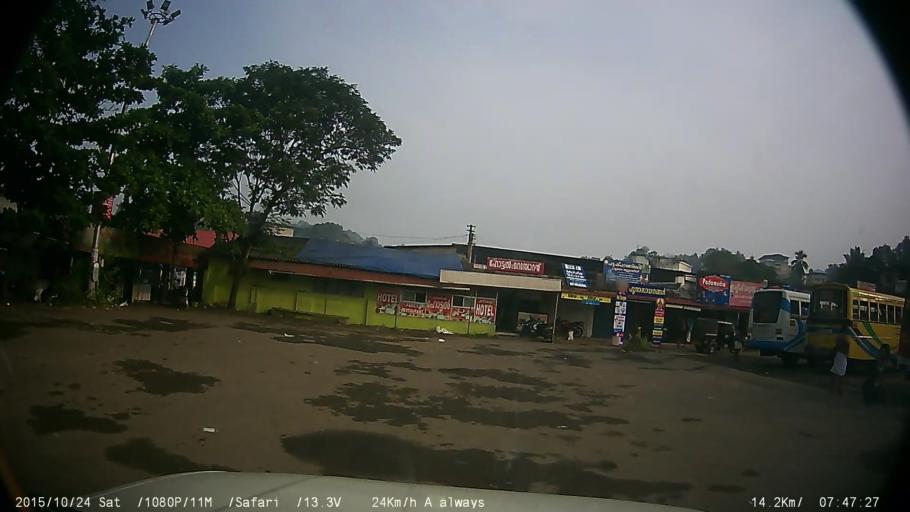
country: IN
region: Kerala
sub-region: Ernakulam
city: Piravam
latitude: 9.8633
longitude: 76.5933
